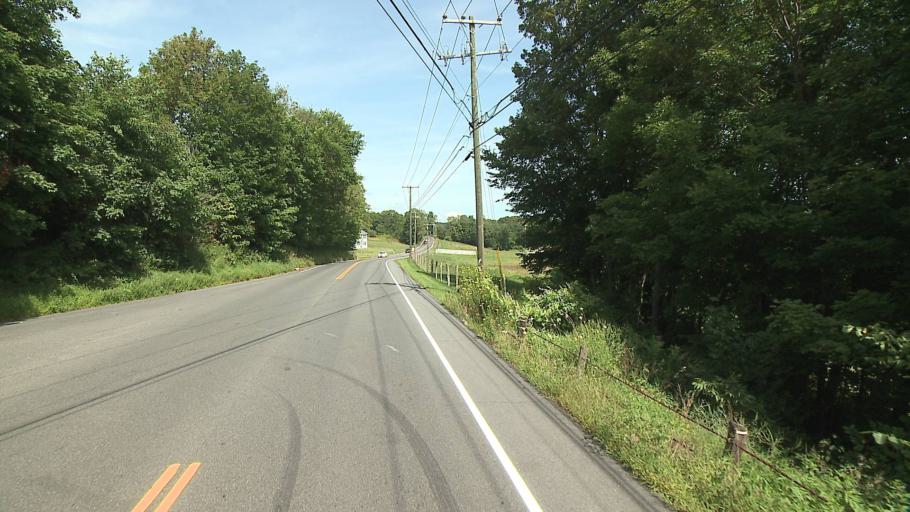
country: US
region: Connecticut
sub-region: Litchfield County
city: Bethlehem Village
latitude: 41.6014
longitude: -73.1746
